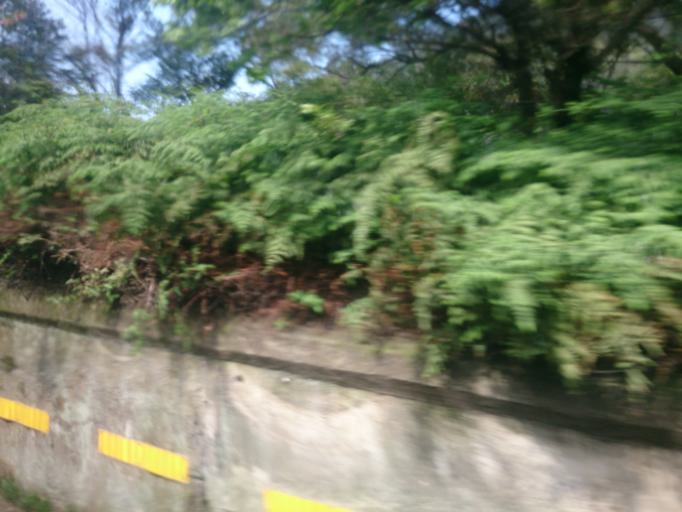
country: TW
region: Taipei
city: Taipei
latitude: 25.1636
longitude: 121.5447
